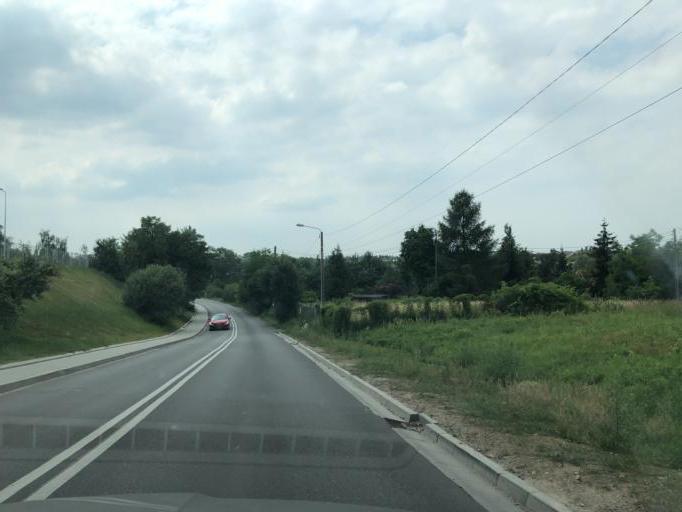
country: PL
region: Lesser Poland Voivodeship
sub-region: Powiat wielicki
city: Wieliczka
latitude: 49.9890
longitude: 20.0416
